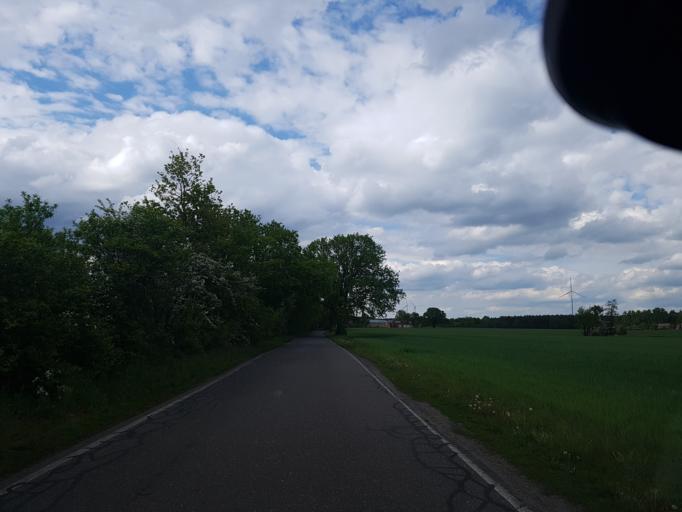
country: DE
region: Brandenburg
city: Grossraschen
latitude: 51.5809
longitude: 14.0624
